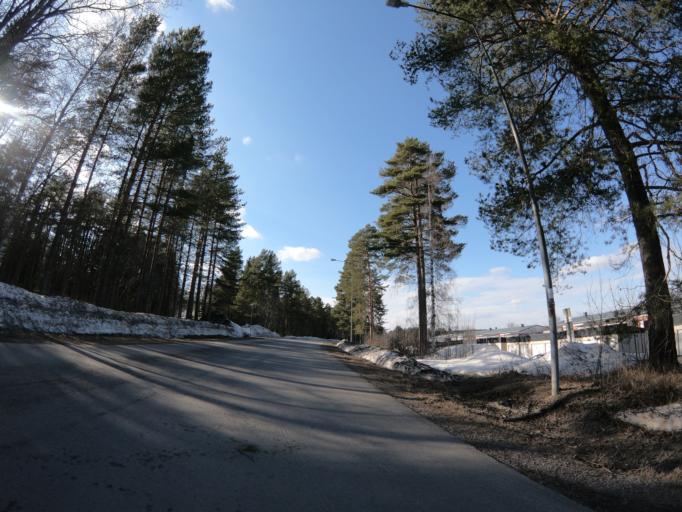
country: SE
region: Vaesterbotten
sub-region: Umea Kommun
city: Ersmark
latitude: 63.8443
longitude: 20.3015
